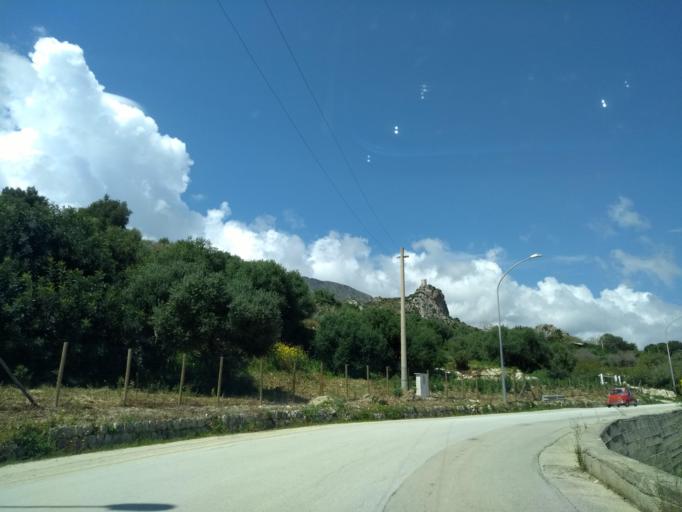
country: IT
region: Sicily
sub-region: Trapani
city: Castellammare del Golfo
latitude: 38.0659
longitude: 12.8194
